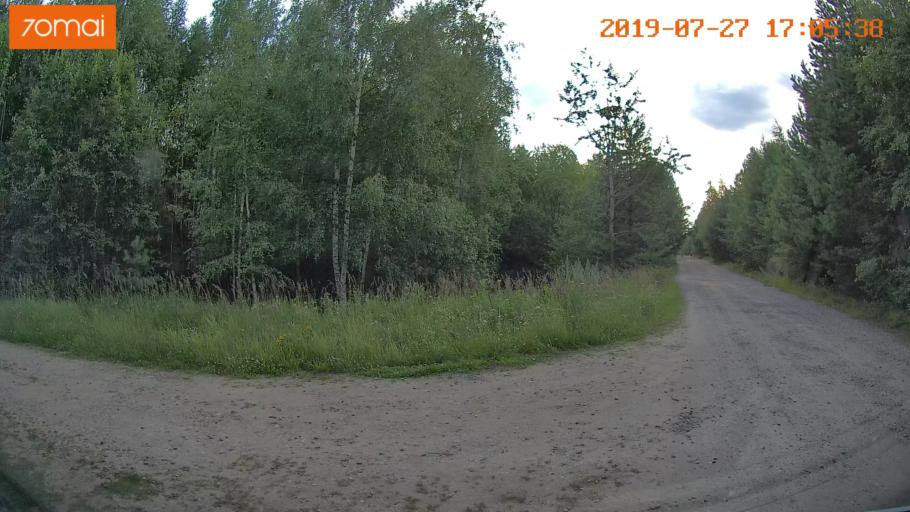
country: RU
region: Ivanovo
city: Novo-Talitsy
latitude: 57.0874
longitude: 40.8461
